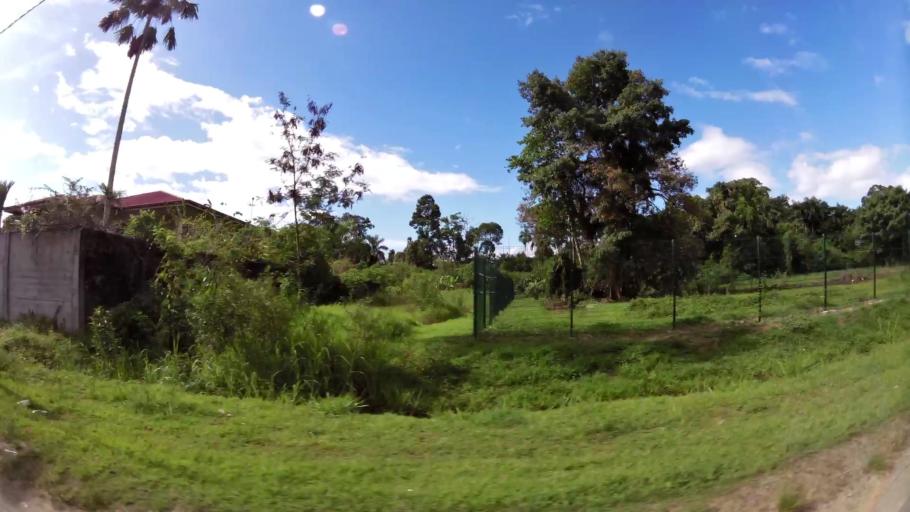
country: SR
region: Paramaribo
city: Paramaribo
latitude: 5.8383
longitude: -55.1611
